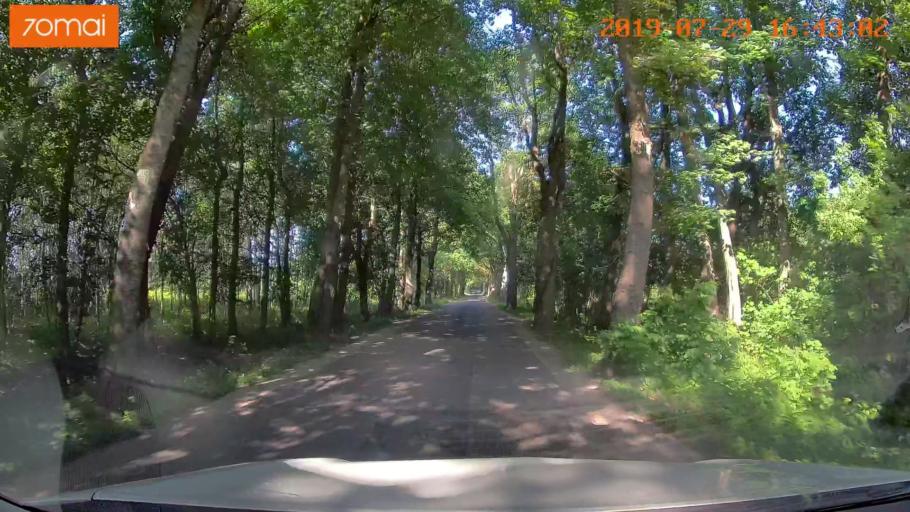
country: RU
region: Kaliningrad
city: Primorsk
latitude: 54.7465
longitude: 20.0799
